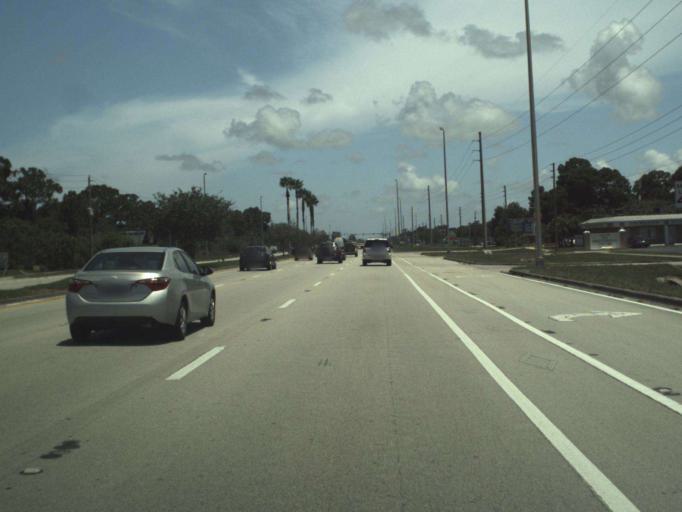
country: US
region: Florida
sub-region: Saint Lucie County
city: River Park
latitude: 27.3154
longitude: -80.3143
